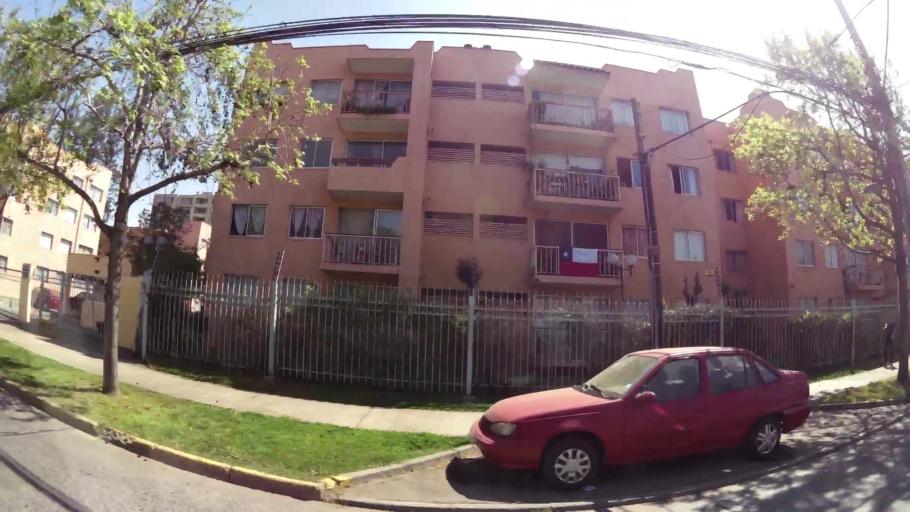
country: CL
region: Santiago Metropolitan
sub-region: Provincia de Santiago
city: Villa Presidente Frei, Nunoa, Santiago, Chile
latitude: -33.4670
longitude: -70.5859
